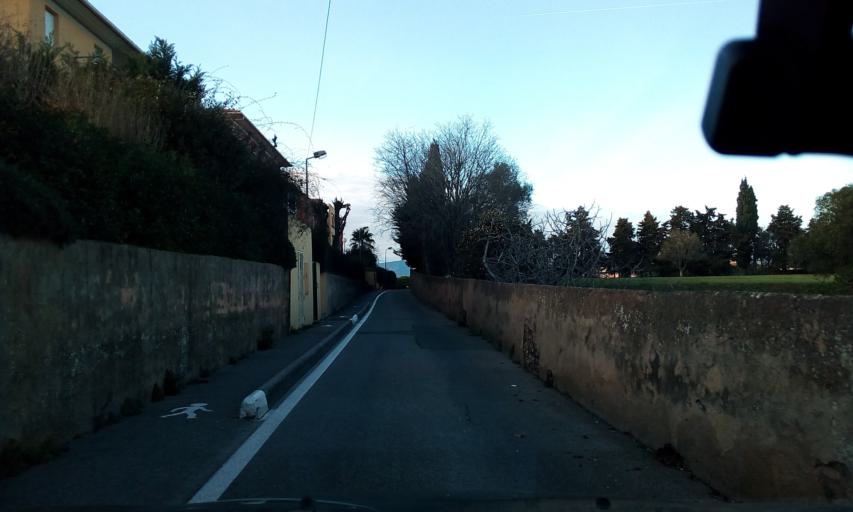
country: FR
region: Provence-Alpes-Cote d'Azur
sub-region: Departement du Var
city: Frejus
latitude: 43.4352
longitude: 6.7353
